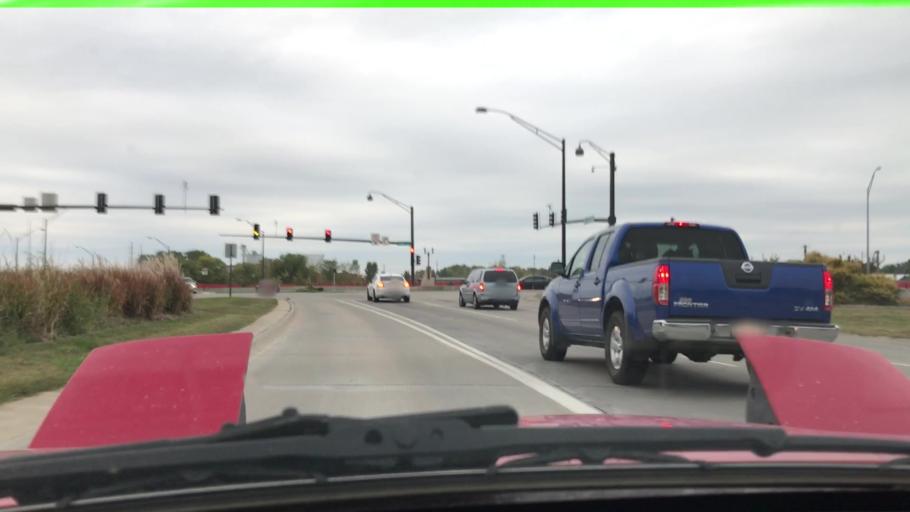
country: US
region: Nebraska
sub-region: Lancaster County
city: Lincoln
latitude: 40.8204
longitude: -96.6923
